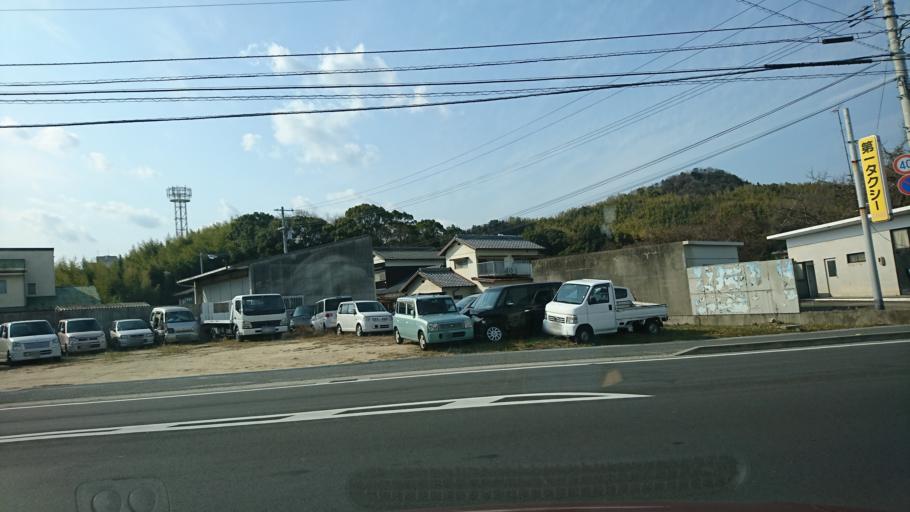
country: JP
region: Ehime
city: Saijo
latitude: 34.0248
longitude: 133.0382
